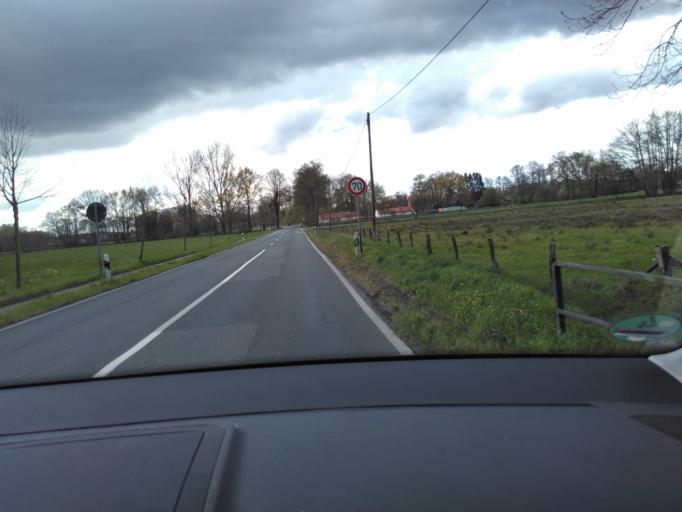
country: DE
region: North Rhine-Westphalia
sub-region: Regierungsbezirk Detmold
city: Verl
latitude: 51.9079
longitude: 8.4653
